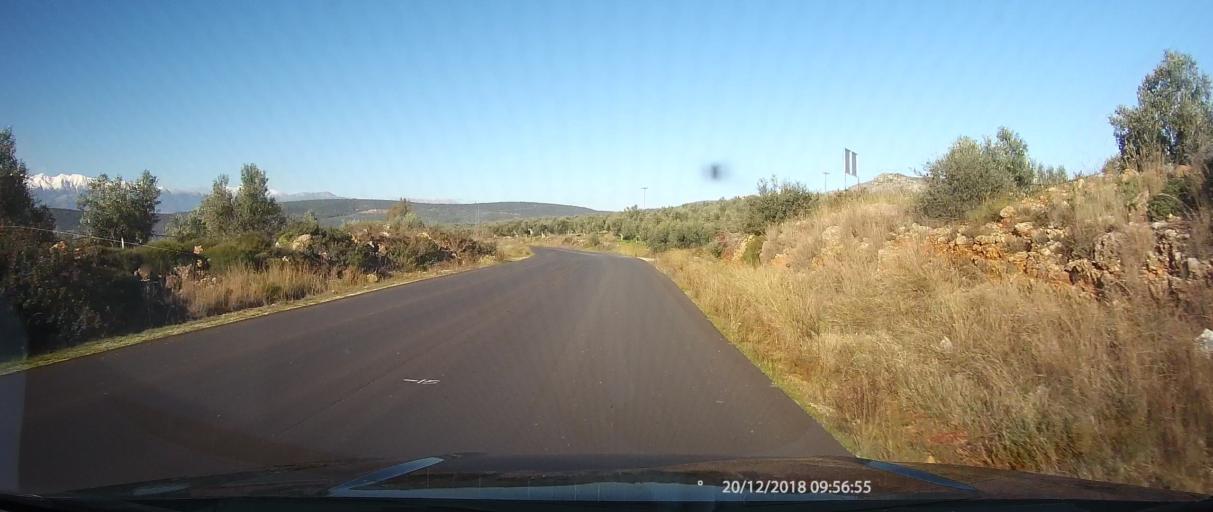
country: GR
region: Peloponnese
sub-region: Nomos Lakonias
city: Yerakion
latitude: 37.0204
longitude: 22.6054
